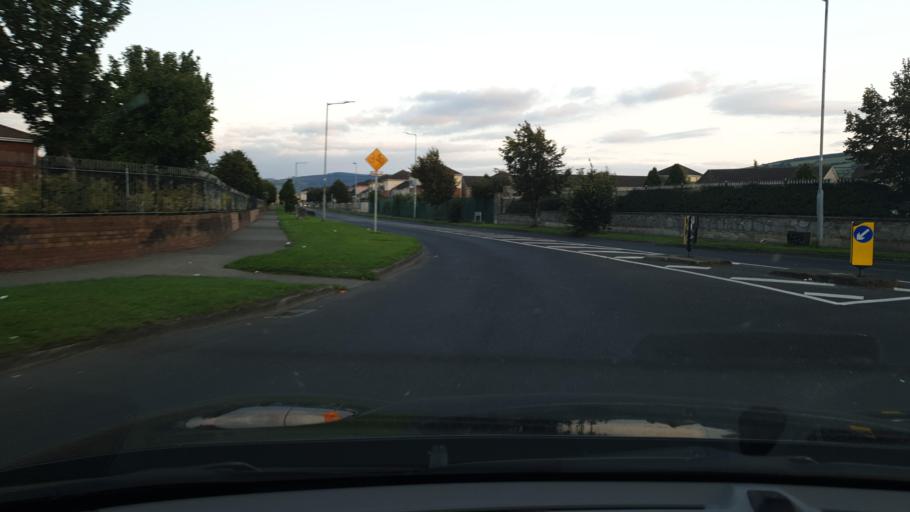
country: IE
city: Jobstown
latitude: 53.2856
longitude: -6.4076
